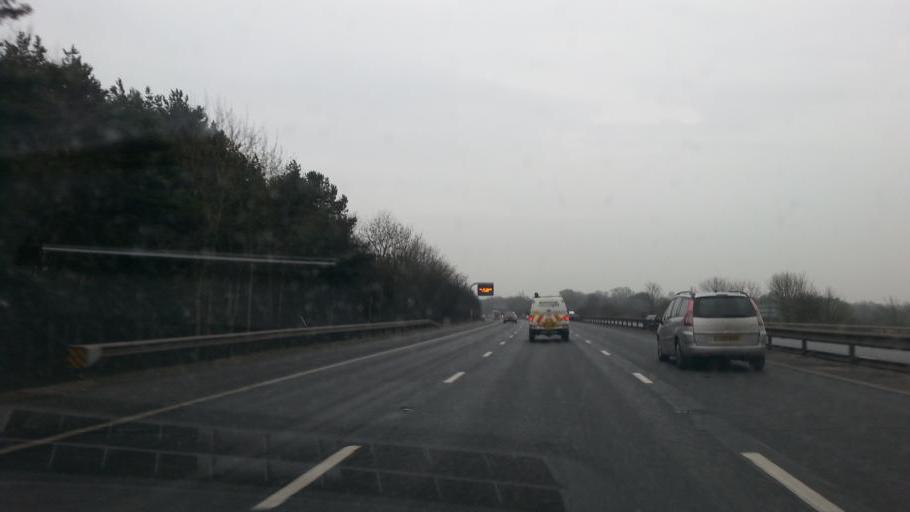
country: GB
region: England
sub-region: Essex
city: Harlow
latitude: 51.7502
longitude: 0.1435
